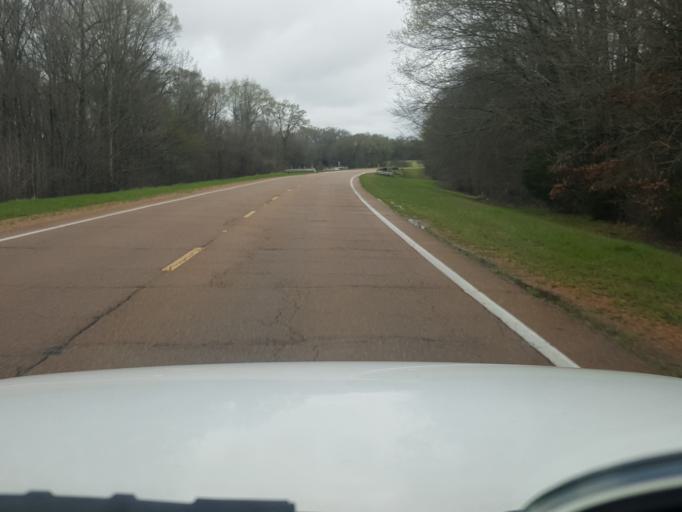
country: US
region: Mississippi
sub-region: Madison County
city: Canton
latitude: 32.7400
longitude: -90.1296
